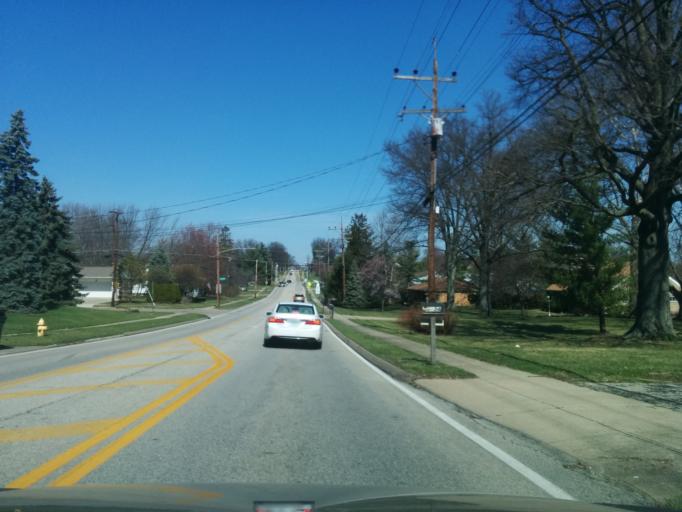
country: US
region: Ohio
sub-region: Hamilton County
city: Groesbeck
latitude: 39.2284
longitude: -84.5994
